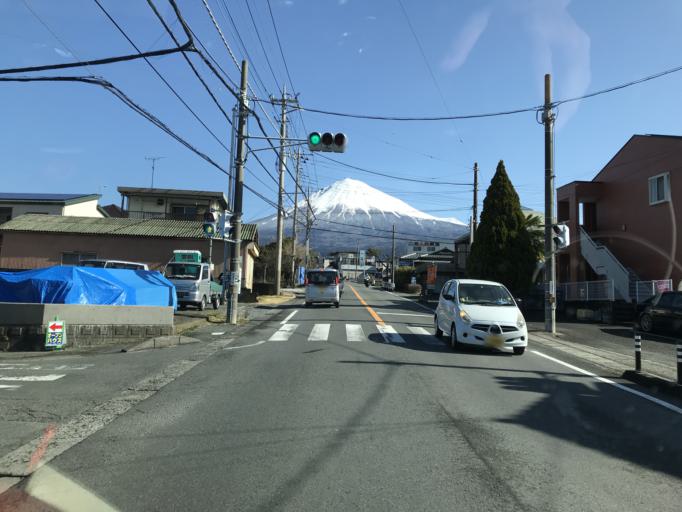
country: JP
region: Shizuoka
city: Fujinomiya
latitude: 35.2481
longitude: 138.6261
